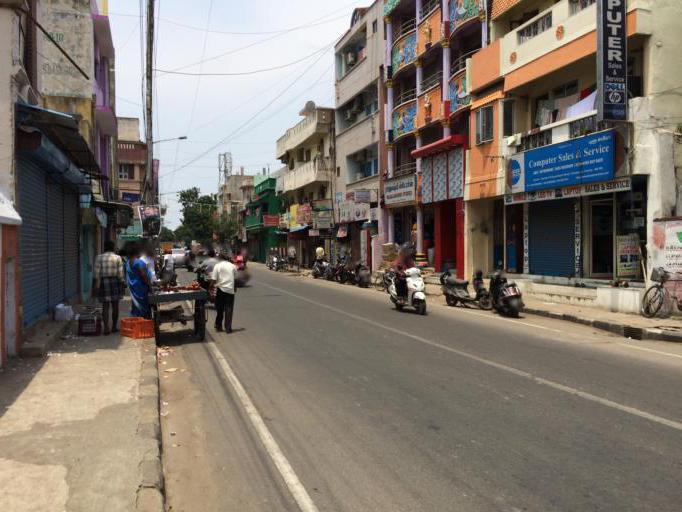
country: IN
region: Tamil Nadu
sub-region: Chennai
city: Chennai
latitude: 13.0759
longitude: 80.2677
